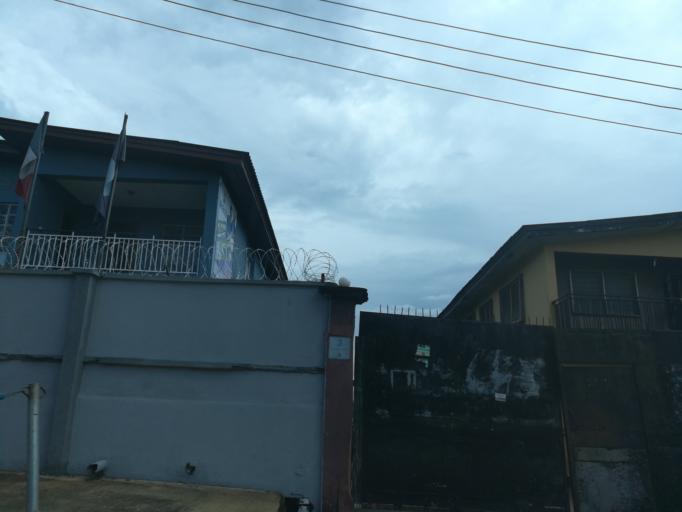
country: NG
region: Lagos
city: Agege
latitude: 6.6050
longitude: 3.3244
